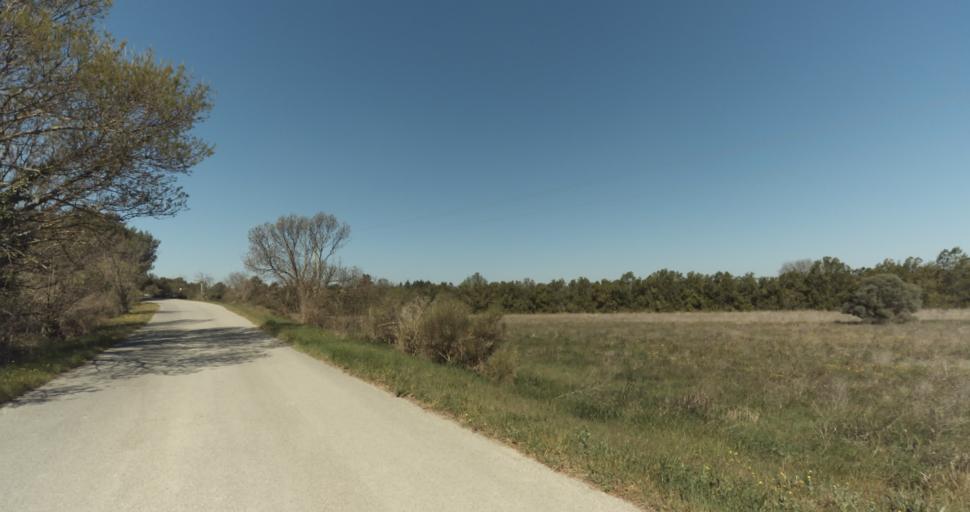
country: FR
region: Provence-Alpes-Cote d'Azur
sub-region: Departement des Bouches-du-Rhone
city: Pelissanne
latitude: 43.6122
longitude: 5.1465
